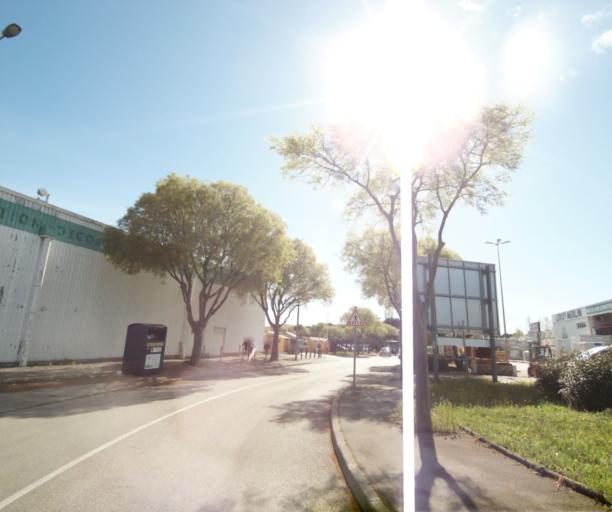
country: FR
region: Languedoc-Roussillon
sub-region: Departement de l'Herault
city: Saint-Jean-de-Vedas
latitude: 43.5704
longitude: 3.8436
